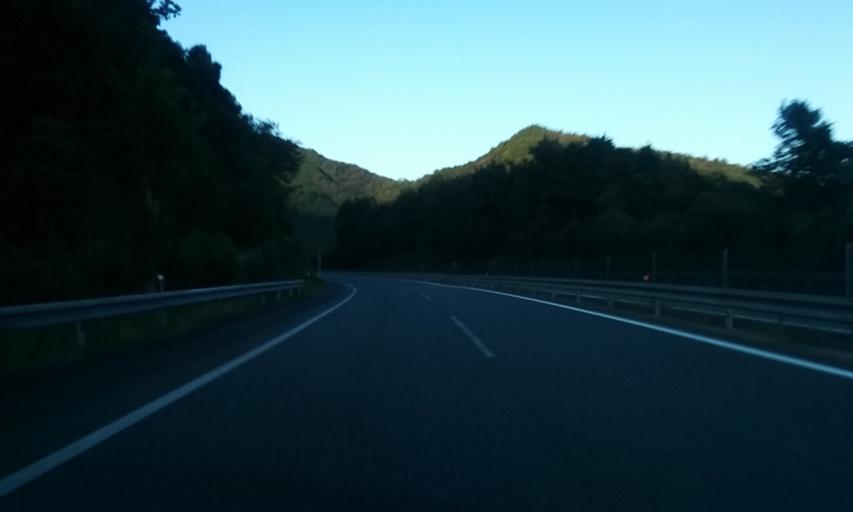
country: JP
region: Kyoto
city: Fukuchiyama
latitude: 35.2051
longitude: 135.1618
